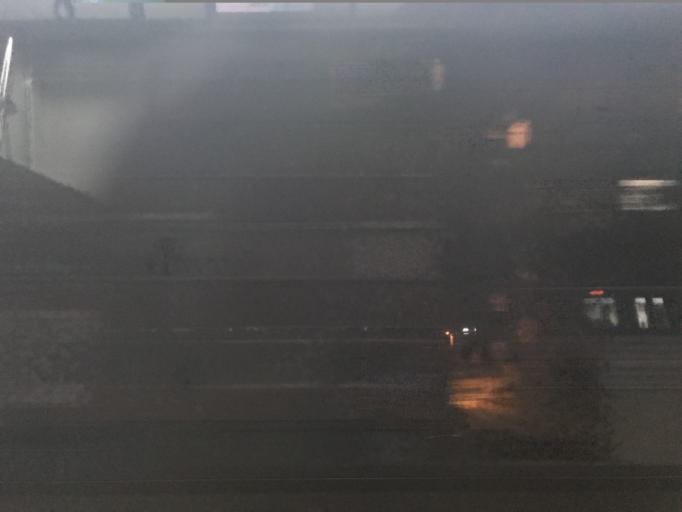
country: TR
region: Istanbul
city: Maltepe
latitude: 40.8855
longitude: 29.2004
